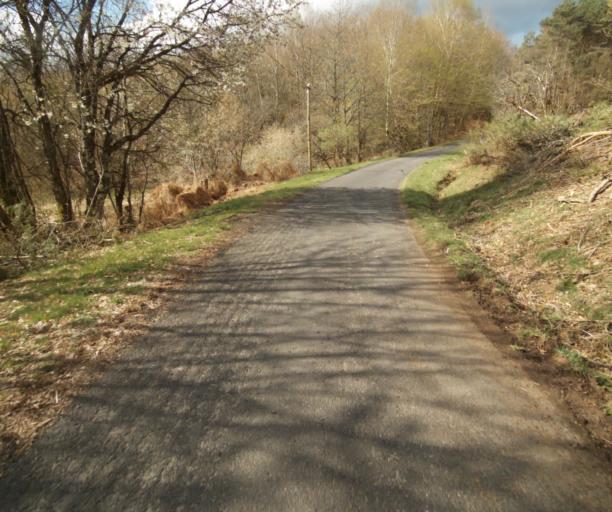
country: FR
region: Limousin
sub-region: Departement de la Correze
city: Argentat
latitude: 45.2357
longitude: 1.9510
